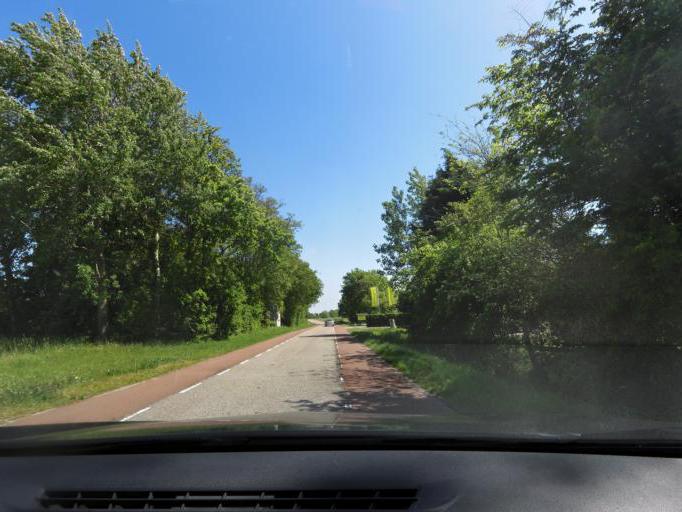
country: NL
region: South Holland
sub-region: Gemeente Goeree-Overflakkee
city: Goedereede
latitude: 51.8041
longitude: 4.0111
